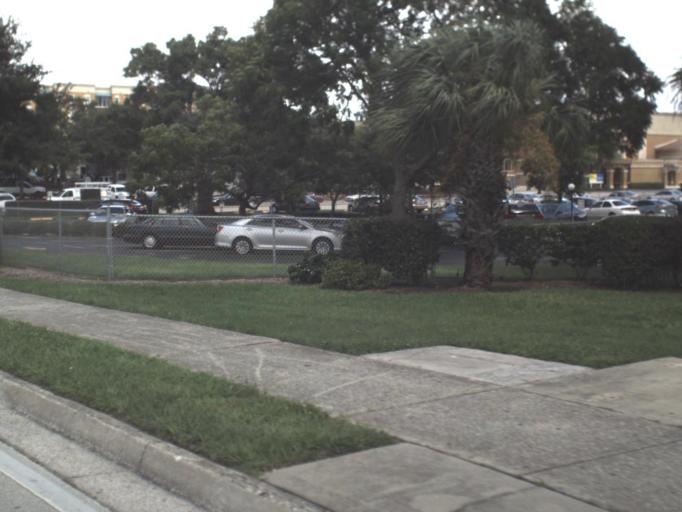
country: US
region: Florida
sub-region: Sarasota County
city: Sarasota
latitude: 27.3442
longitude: -82.5467
